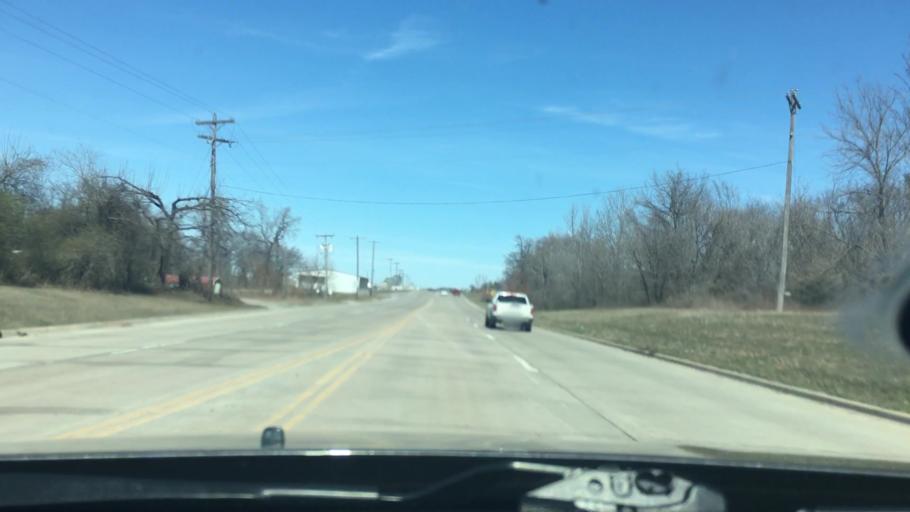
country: US
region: Oklahoma
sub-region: Pontotoc County
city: Ada
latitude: 34.7655
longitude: -96.7006
